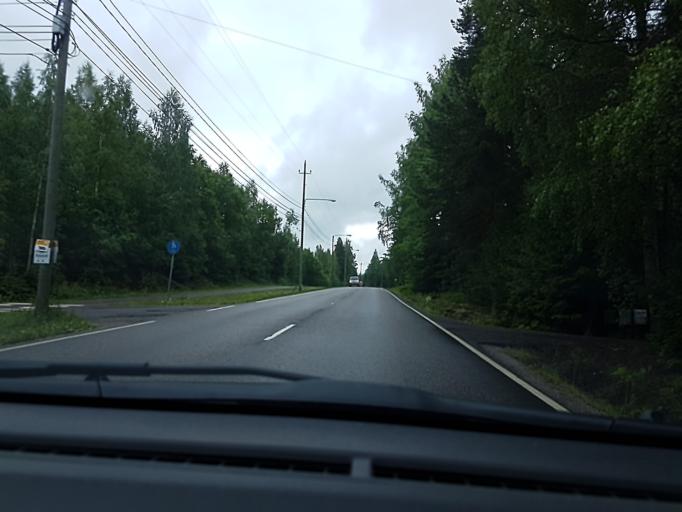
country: FI
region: Uusimaa
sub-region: Helsinki
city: Pornainen
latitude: 60.4666
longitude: 25.3882
